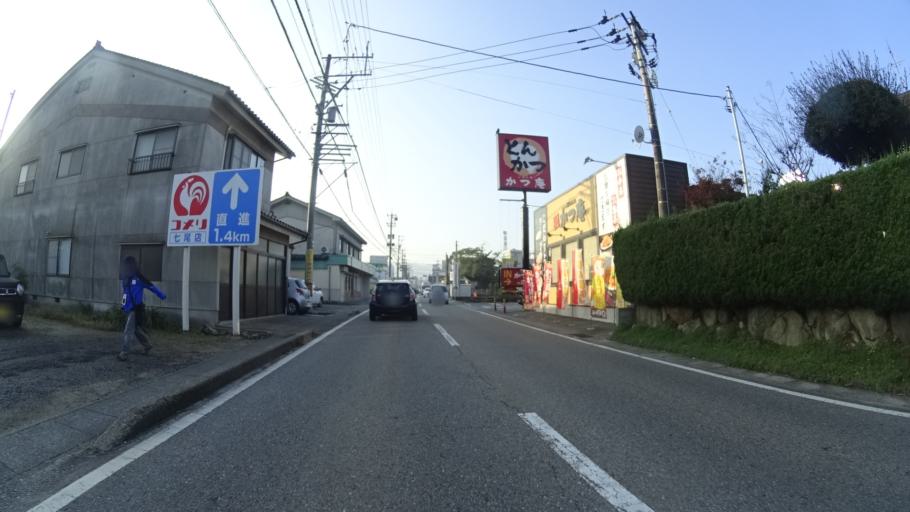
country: JP
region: Ishikawa
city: Nanao
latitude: 37.0385
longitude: 136.9692
